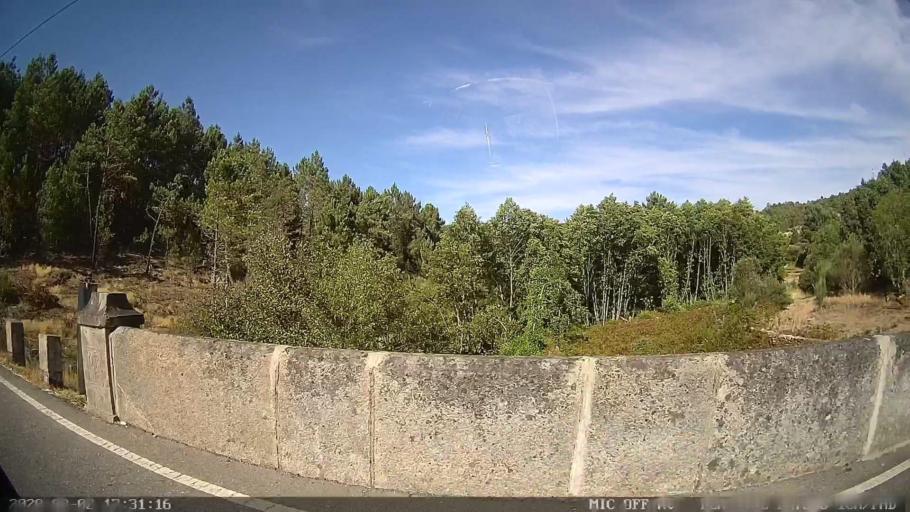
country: PT
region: Vila Real
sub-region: Sabrosa
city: Sabrosa
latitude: 41.3560
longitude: -7.5767
